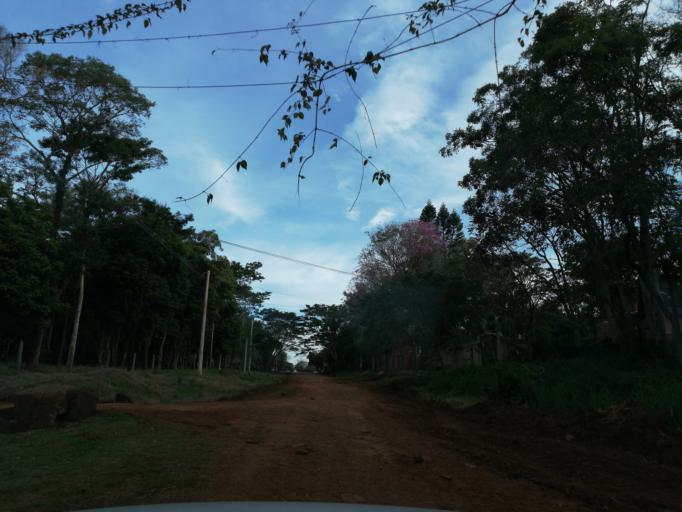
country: AR
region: Misiones
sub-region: Departamento de Capital
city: Posadas
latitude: -27.3554
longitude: -55.9301
